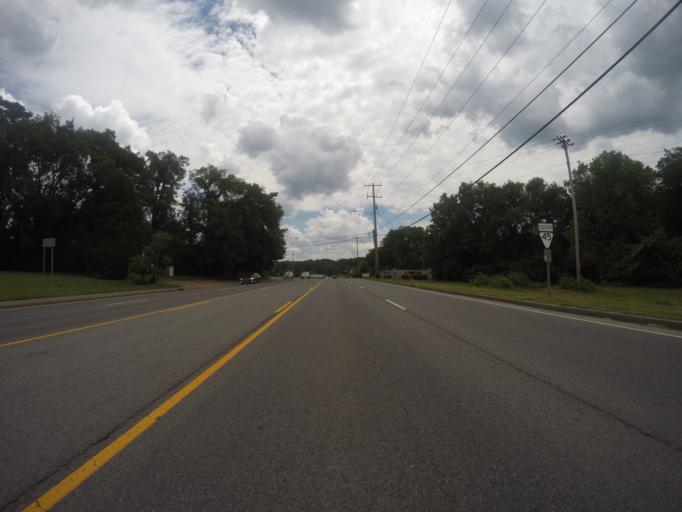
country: US
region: Tennessee
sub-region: Davidson County
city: Lakewood
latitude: 36.2350
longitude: -86.6264
